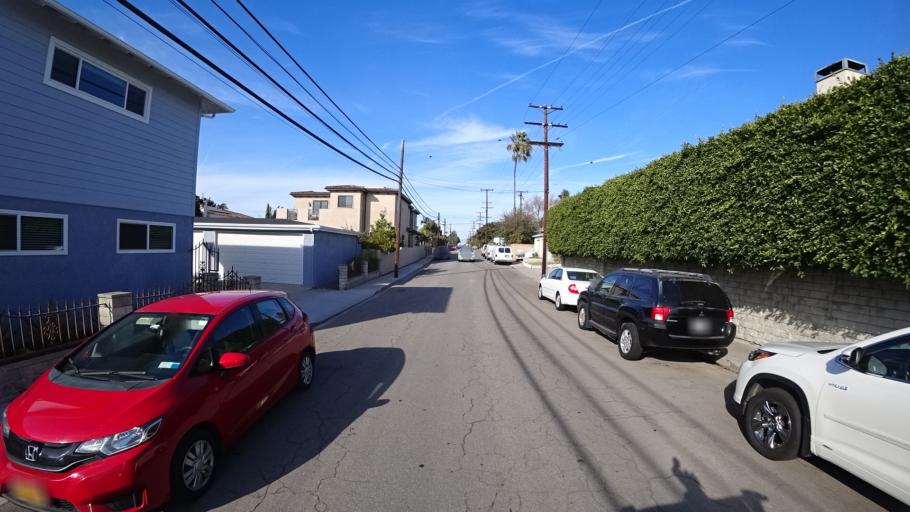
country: US
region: California
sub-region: Los Angeles County
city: Hermosa Beach
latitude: 33.8812
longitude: -118.3808
